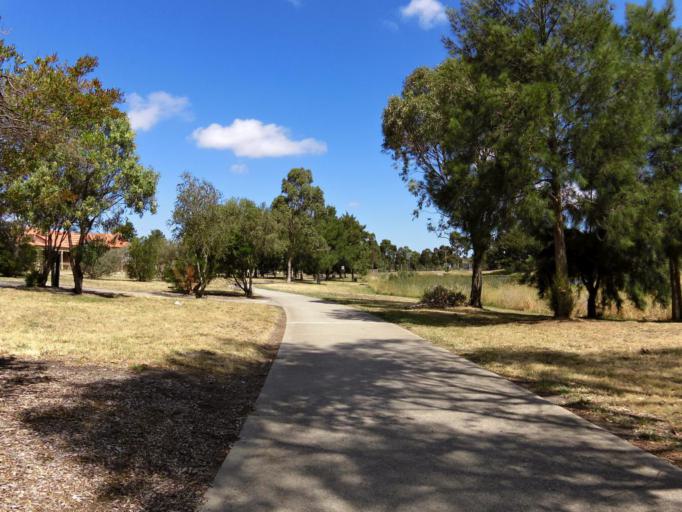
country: AU
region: Victoria
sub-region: Hume
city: Roxburgh Park
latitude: -37.6339
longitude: 144.9224
